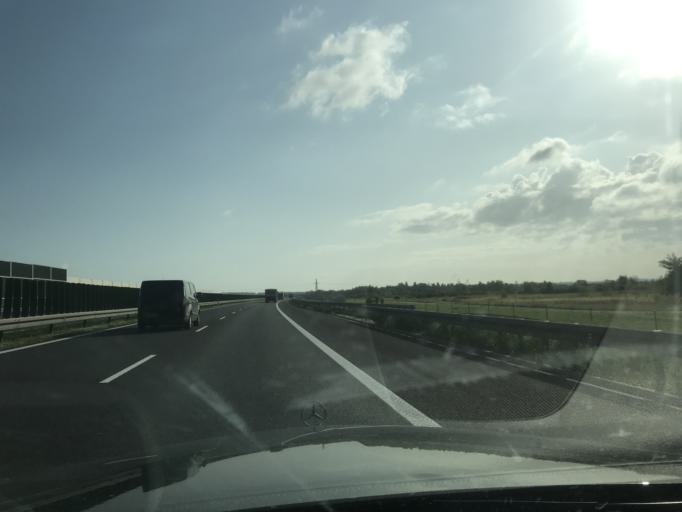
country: PL
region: Lesser Poland Voivodeship
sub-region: Powiat tarnowski
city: Lukowa
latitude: 50.0580
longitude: 20.9302
